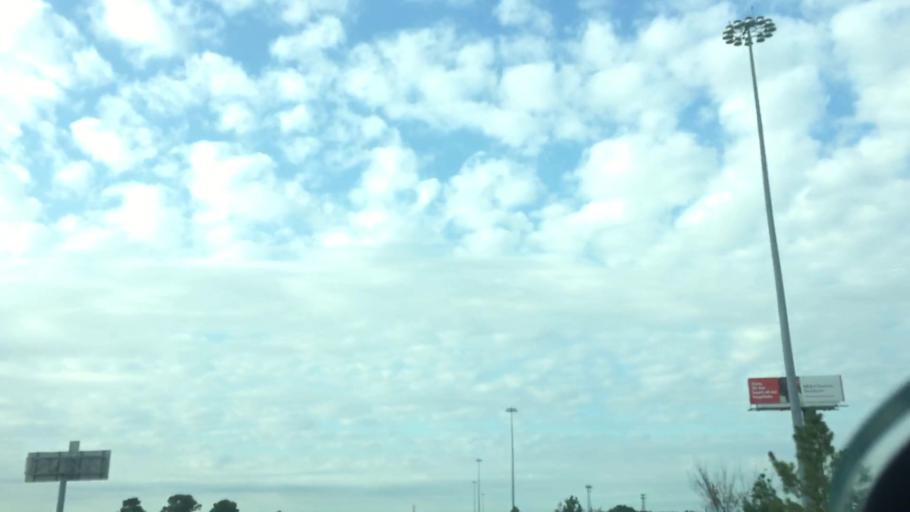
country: US
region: Texas
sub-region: Harris County
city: Oak Cliff Place
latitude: 29.9972
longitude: -95.5795
